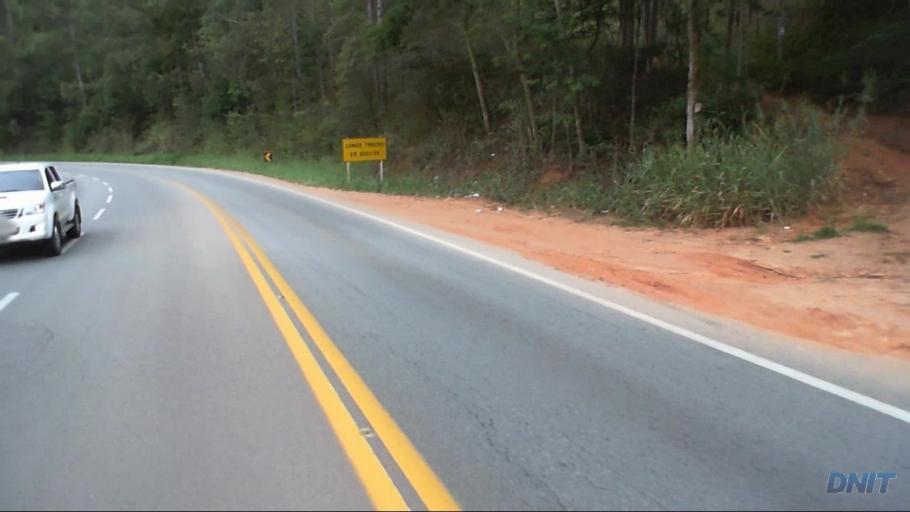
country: BR
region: Minas Gerais
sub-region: Joao Monlevade
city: Joao Monlevade
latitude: -19.8419
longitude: -43.0982
